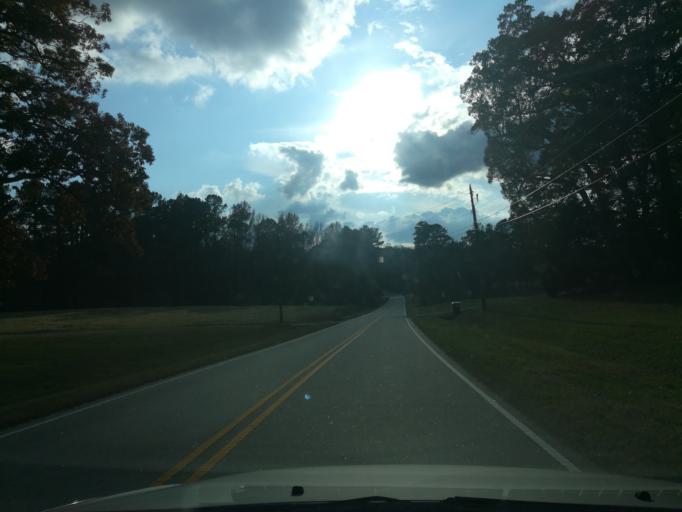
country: US
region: North Carolina
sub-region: Durham County
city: Durham
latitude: 36.0119
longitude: -78.9872
